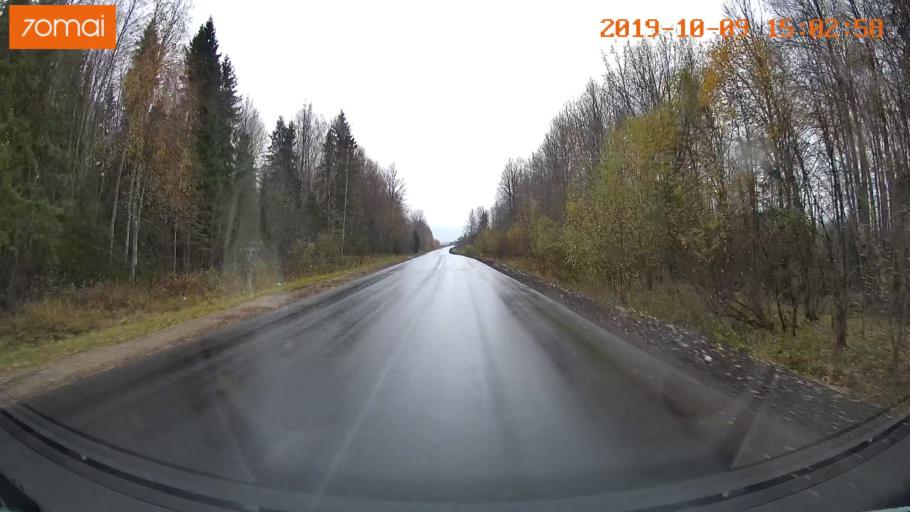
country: RU
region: Kostroma
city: Chistyye Bory
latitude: 58.2779
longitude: 41.6765
